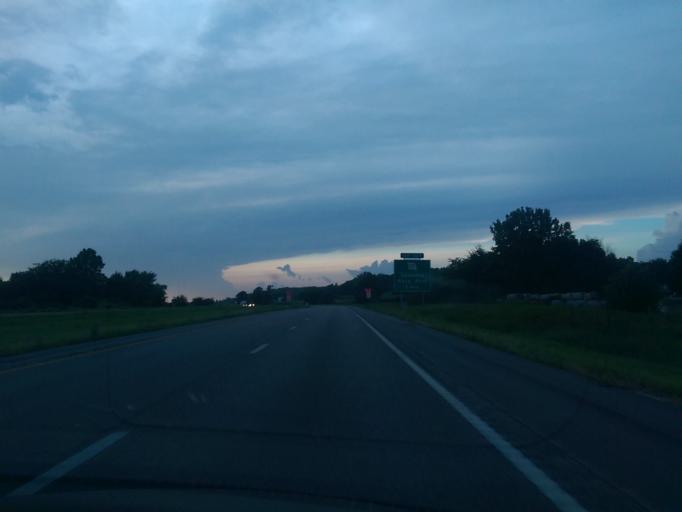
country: US
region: Missouri
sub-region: Atchison County
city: Rock Port
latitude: 40.3543
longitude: -95.5155
